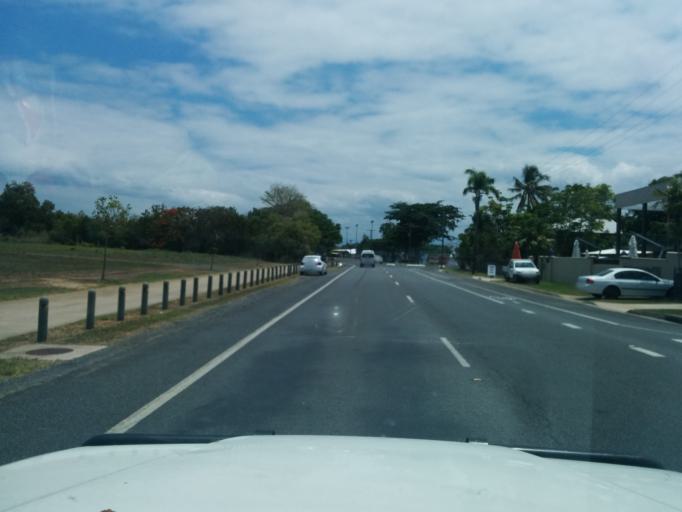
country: AU
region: Queensland
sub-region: Cairns
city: Cairns
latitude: -16.8993
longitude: 145.7584
